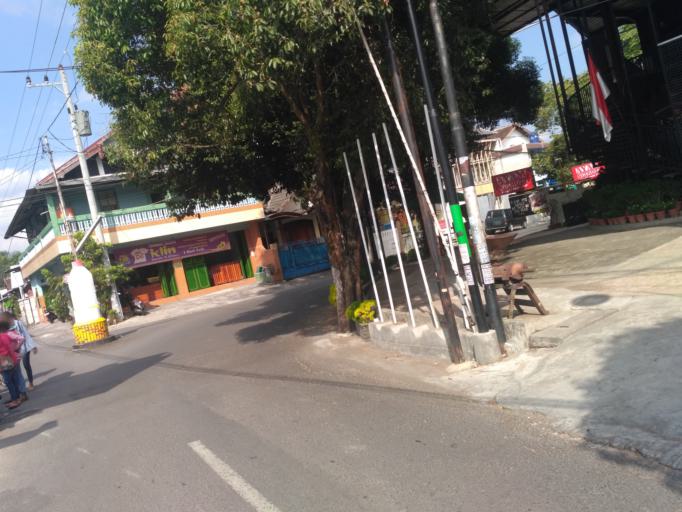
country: ID
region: Daerah Istimewa Yogyakarta
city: Depok
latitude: -7.7775
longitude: 110.4052
